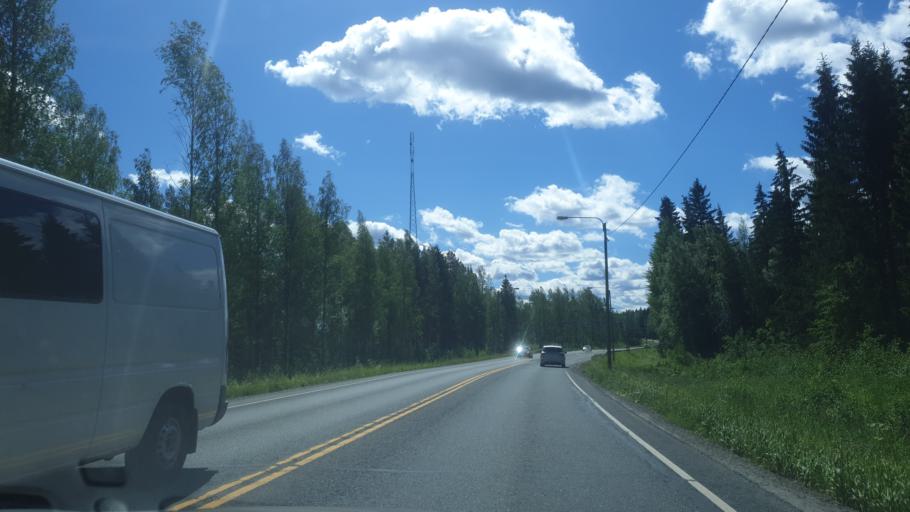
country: FI
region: Northern Savo
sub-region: Varkaus
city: Leppaevirta
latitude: 62.5844
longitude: 27.6053
